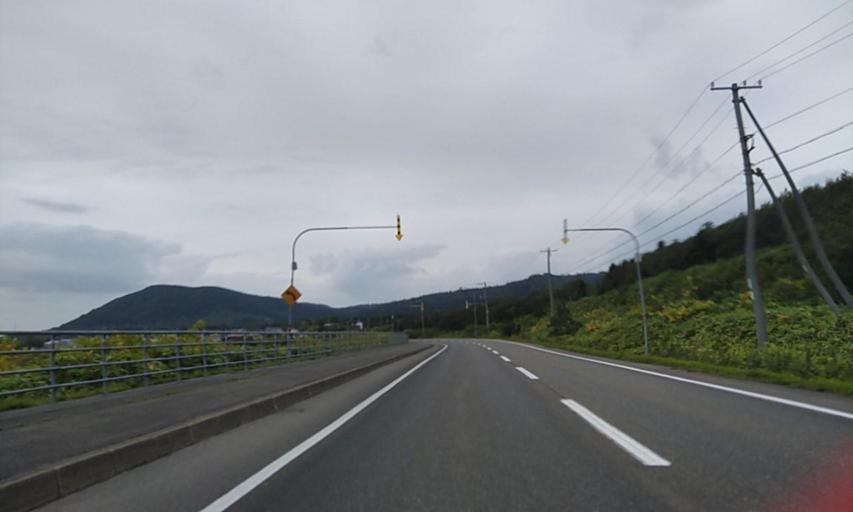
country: JP
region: Hokkaido
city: Nayoro
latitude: 45.0409
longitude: 142.5065
